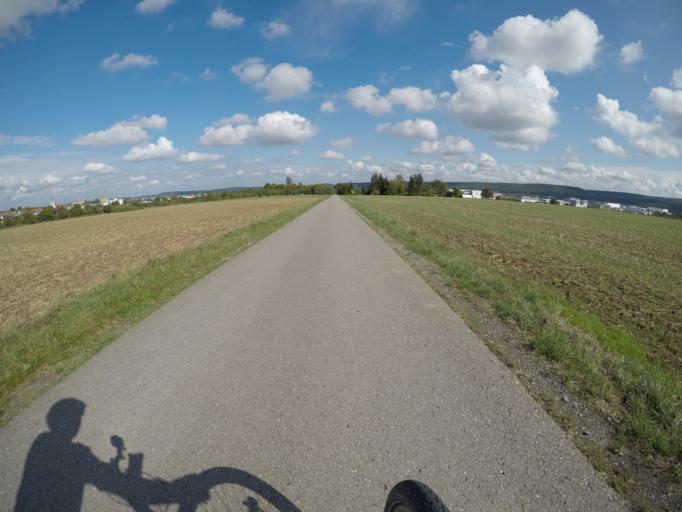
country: DE
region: Baden-Wuerttemberg
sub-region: Regierungsbezirk Stuttgart
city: Nufringen
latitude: 48.6341
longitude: 8.8888
